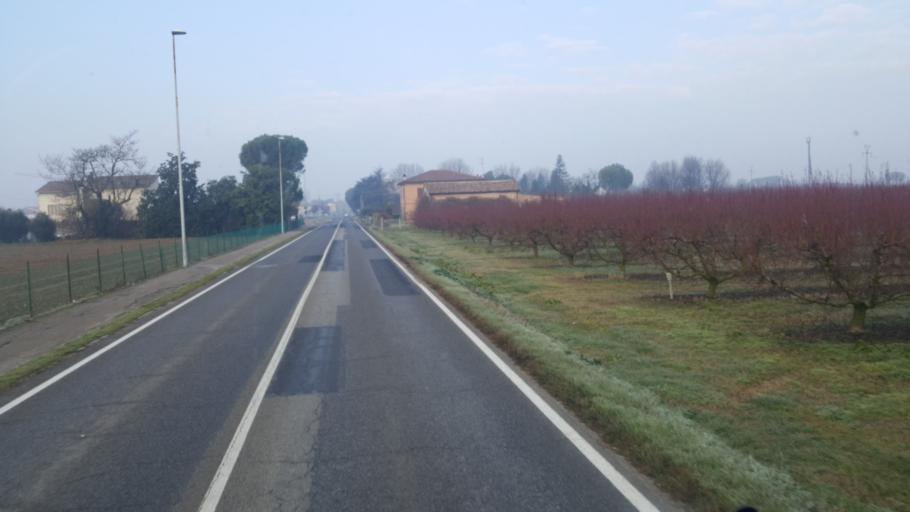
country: IT
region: Emilia-Romagna
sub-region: Provincia di Ravenna
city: Bagnacavallo
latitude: 44.4112
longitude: 11.9904
